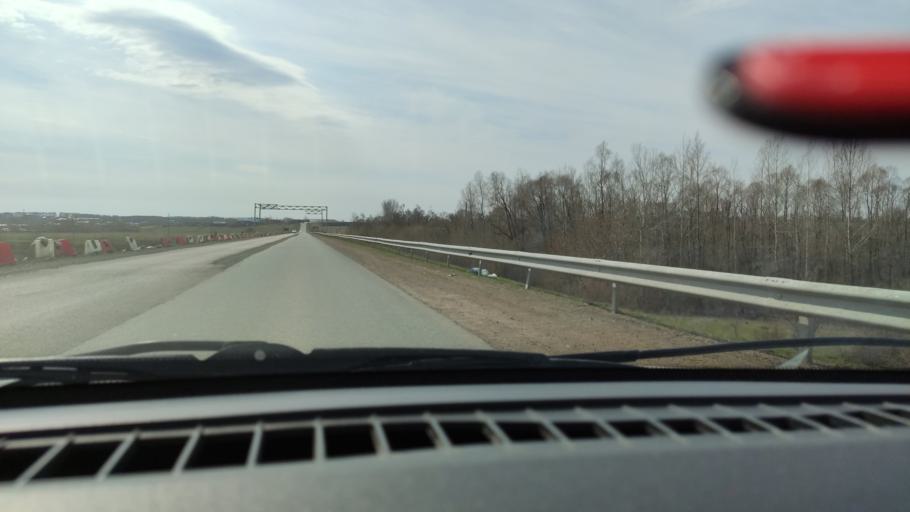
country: RU
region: Bashkortostan
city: Dyurtyuli
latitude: 55.5122
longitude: 54.8360
